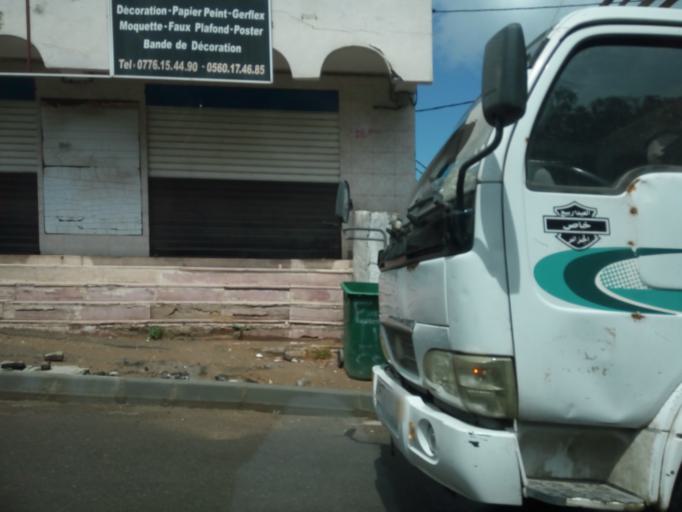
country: DZ
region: Alger
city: Algiers
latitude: 36.7734
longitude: 3.0442
